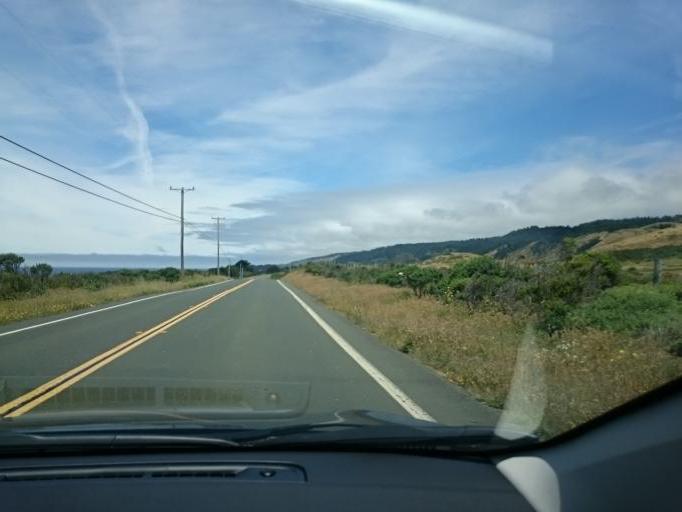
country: US
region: California
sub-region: Mendocino County
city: Fort Bragg
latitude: 39.1164
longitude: -123.7135
